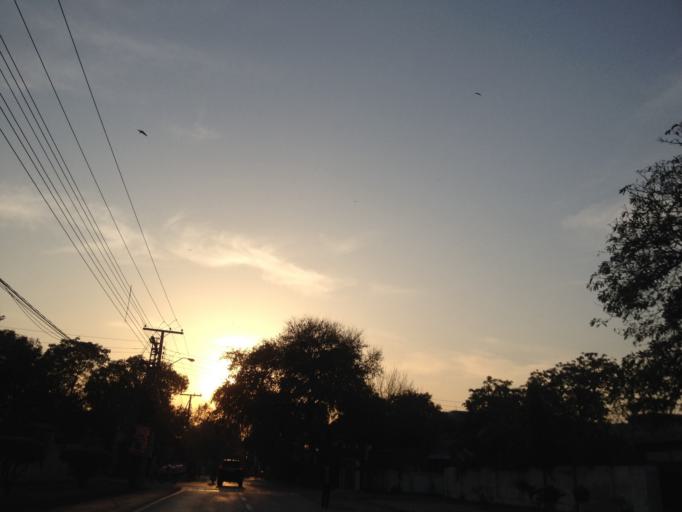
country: PK
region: Punjab
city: Lahore
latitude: 31.4916
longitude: 74.3159
